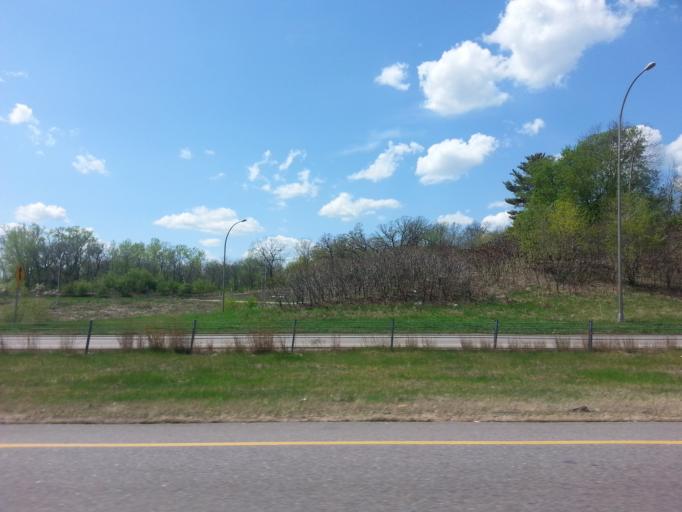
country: US
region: Minnesota
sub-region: Hennepin County
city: Edina
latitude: 44.8383
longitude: -93.3984
